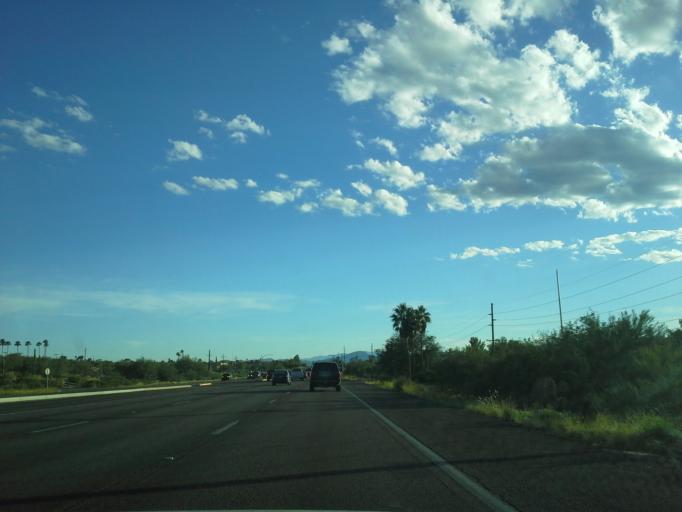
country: US
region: Arizona
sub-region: Pima County
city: Oro Valley
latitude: 32.3698
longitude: -110.9683
